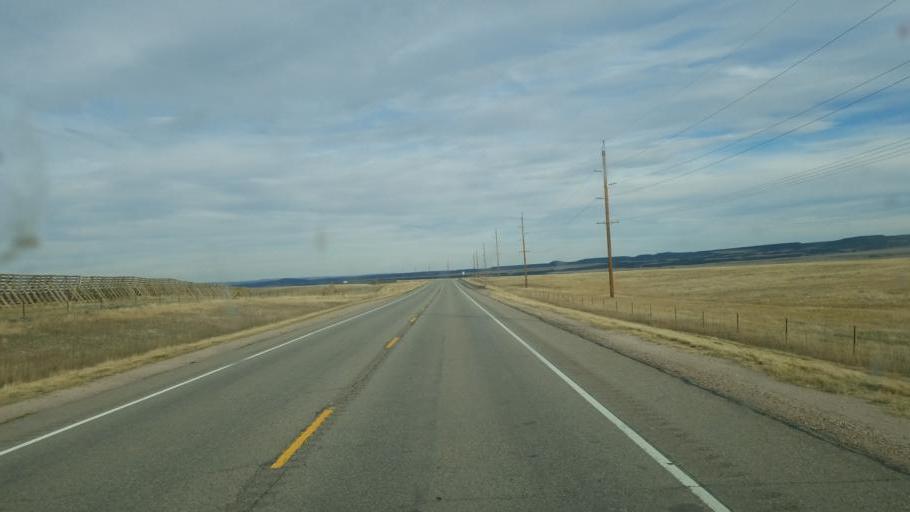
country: US
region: Colorado
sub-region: Huerfano County
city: Walsenburg
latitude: 37.5441
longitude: -105.0119
